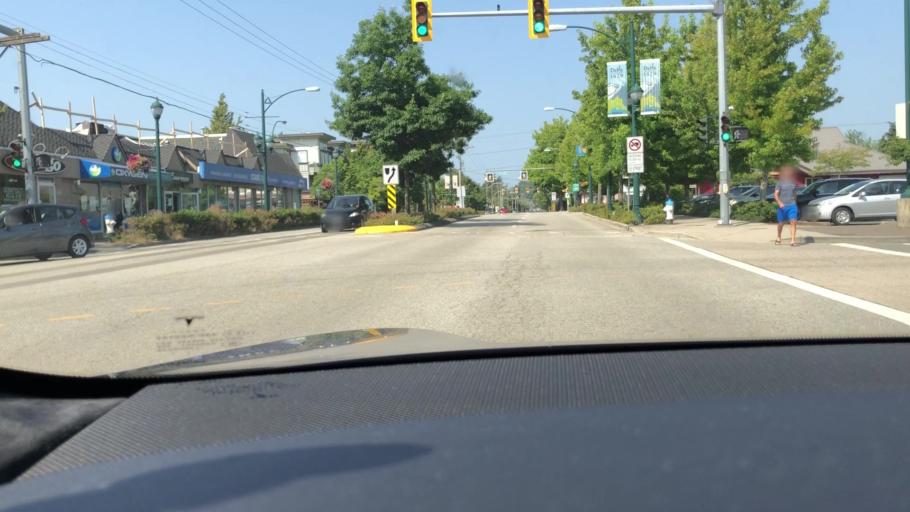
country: US
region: Washington
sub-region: Whatcom County
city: Point Roberts
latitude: 49.0248
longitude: -123.0705
